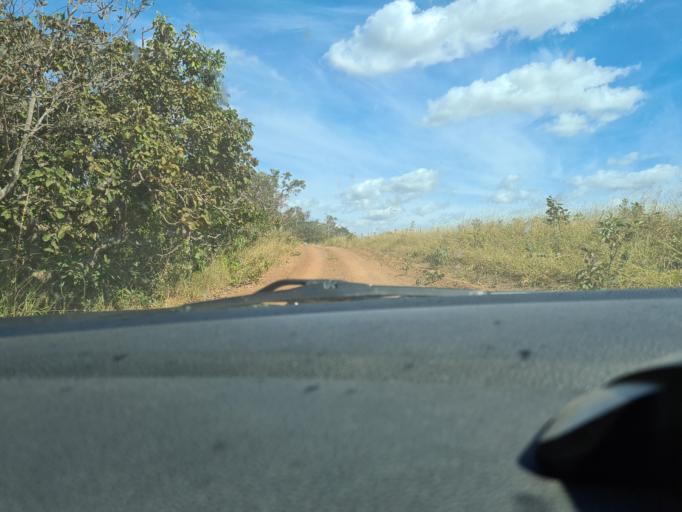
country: BR
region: Goias
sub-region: Silvania
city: Silvania
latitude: -16.5302
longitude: -48.5511
